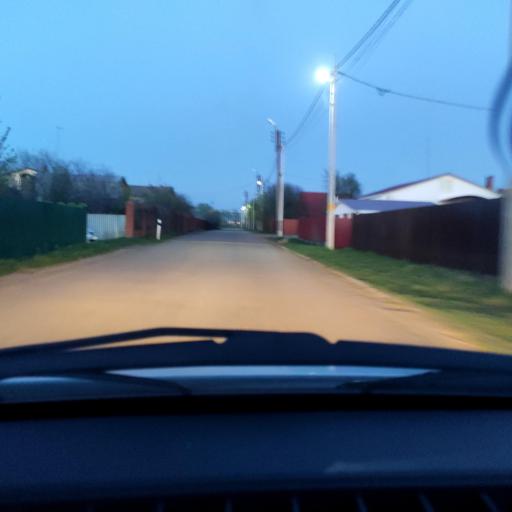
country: RU
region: Bashkortostan
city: Mikhaylovka
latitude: 54.8658
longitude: 55.7406
